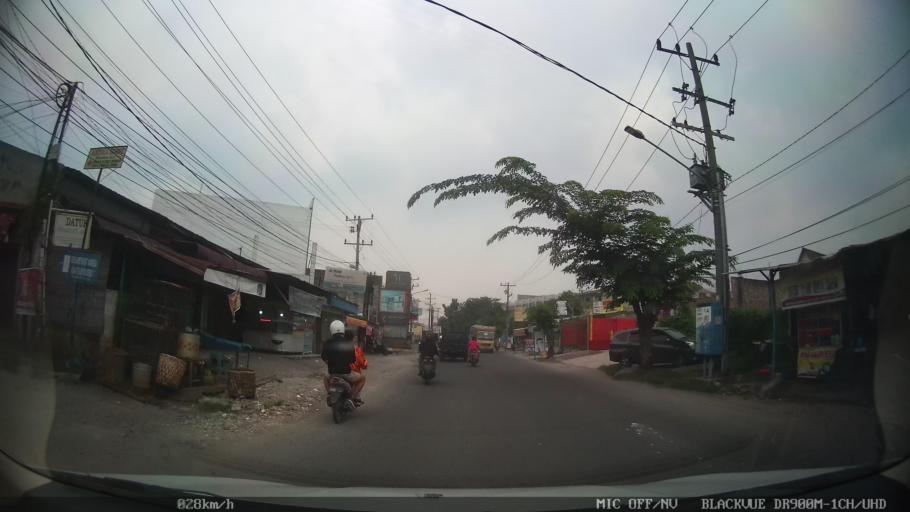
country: ID
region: North Sumatra
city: Medan
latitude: 3.5566
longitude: 98.7178
